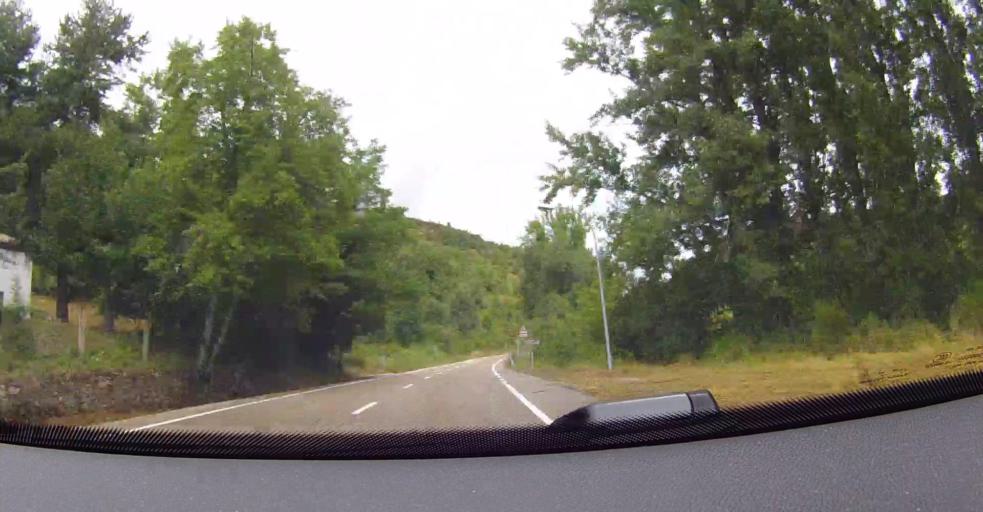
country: ES
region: Castille and Leon
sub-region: Provincia de Leon
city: Bonar
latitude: 42.8987
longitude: -5.3148
